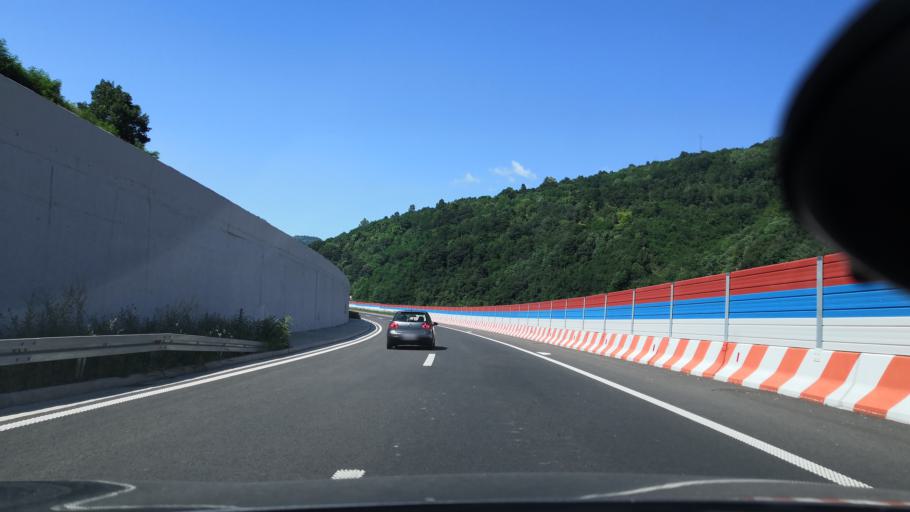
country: RS
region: Central Serbia
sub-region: Pcinjski Okrug
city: Vladicin Han
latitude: 42.7786
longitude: 22.0914
